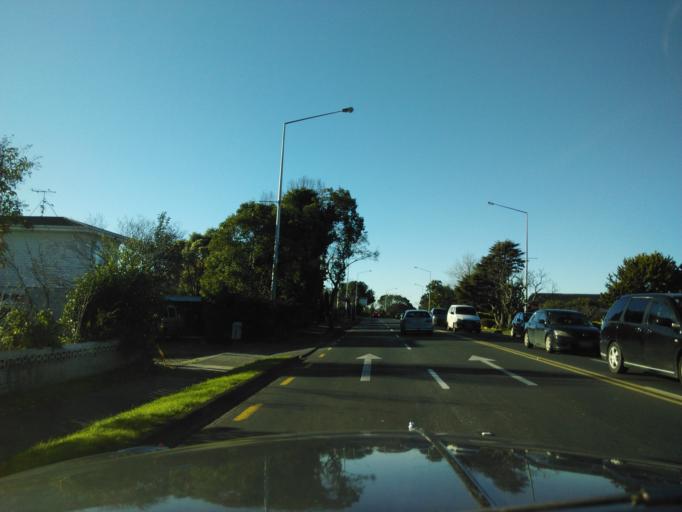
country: NZ
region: Auckland
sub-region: Auckland
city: Rosebank
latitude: -36.8623
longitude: 174.6491
